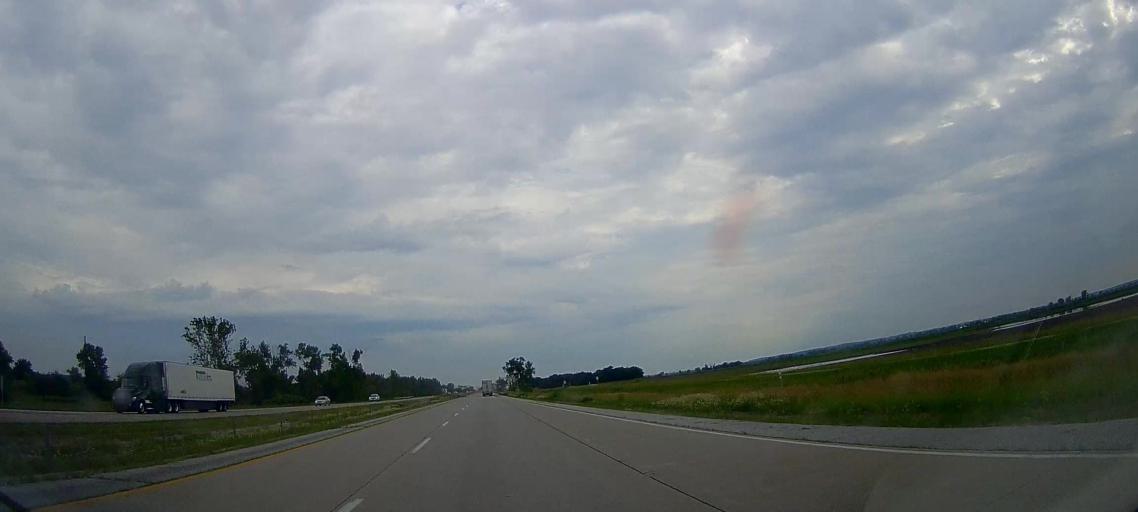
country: US
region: Iowa
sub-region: Harrison County
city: Missouri Valley
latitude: 41.4859
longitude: -95.9009
